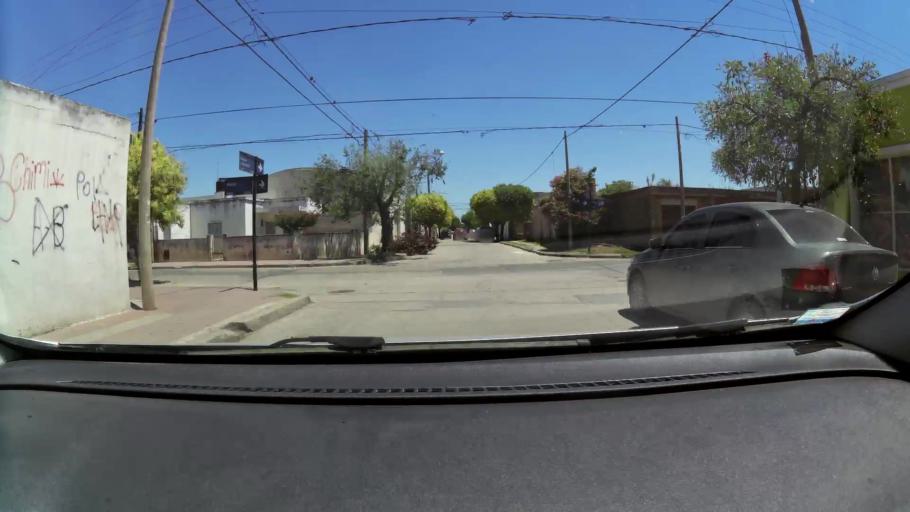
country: AR
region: Cordoba
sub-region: Departamento de Capital
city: Cordoba
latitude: -31.3795
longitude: -64.1332
